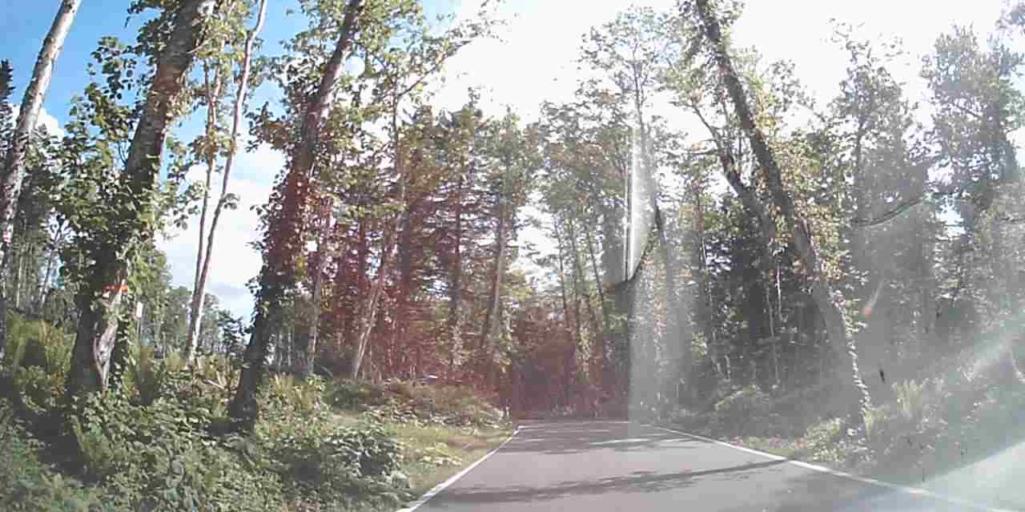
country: JP
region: Hokkaido
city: Shiraoi
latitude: 42.7249
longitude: 141.4139
